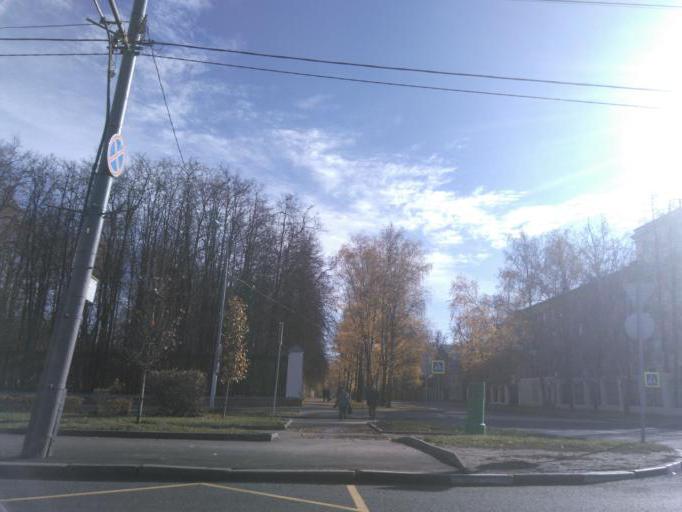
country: RU
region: Moskovskaya
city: Leninskiye Gory
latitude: 55.6998
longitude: 37.5664
